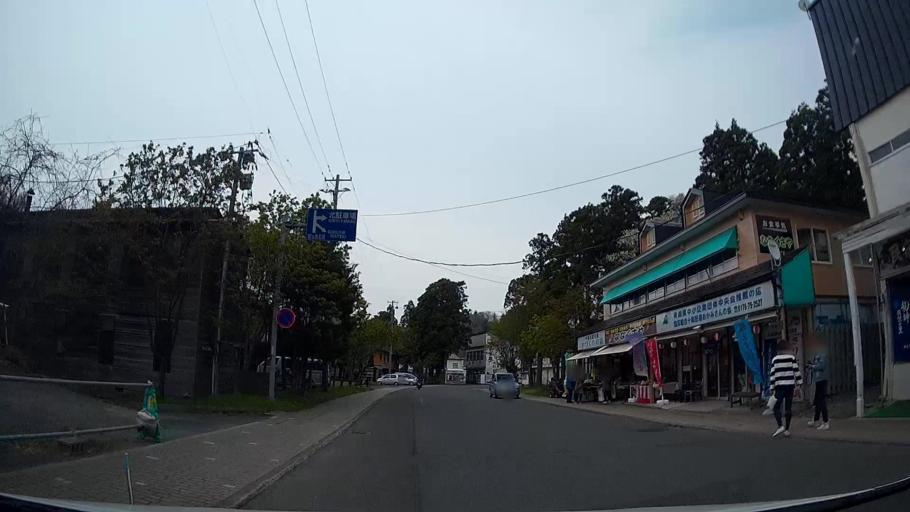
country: JP
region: Akita
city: Hanawa
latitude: 40.4276
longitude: 140.8940
